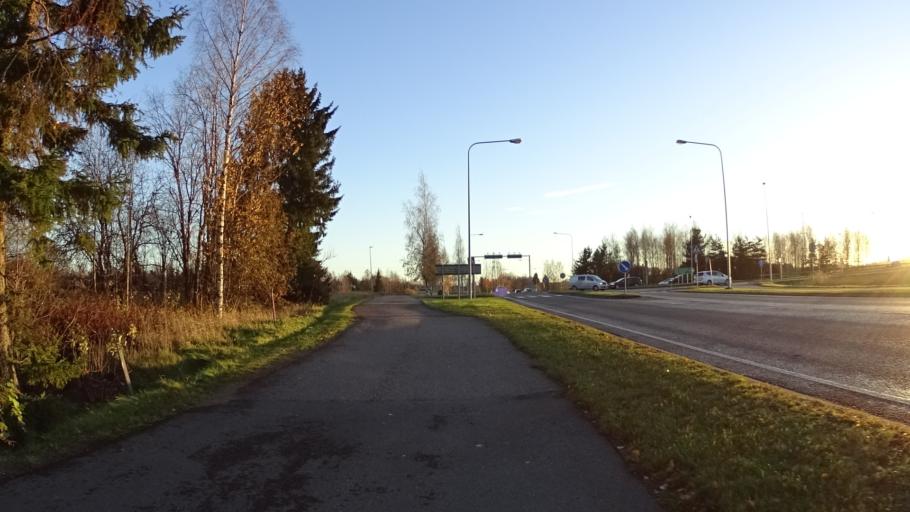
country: FI
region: Uusimaa
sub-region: Helsinki
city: Vantaa
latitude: 60.2695
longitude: 24.9746
